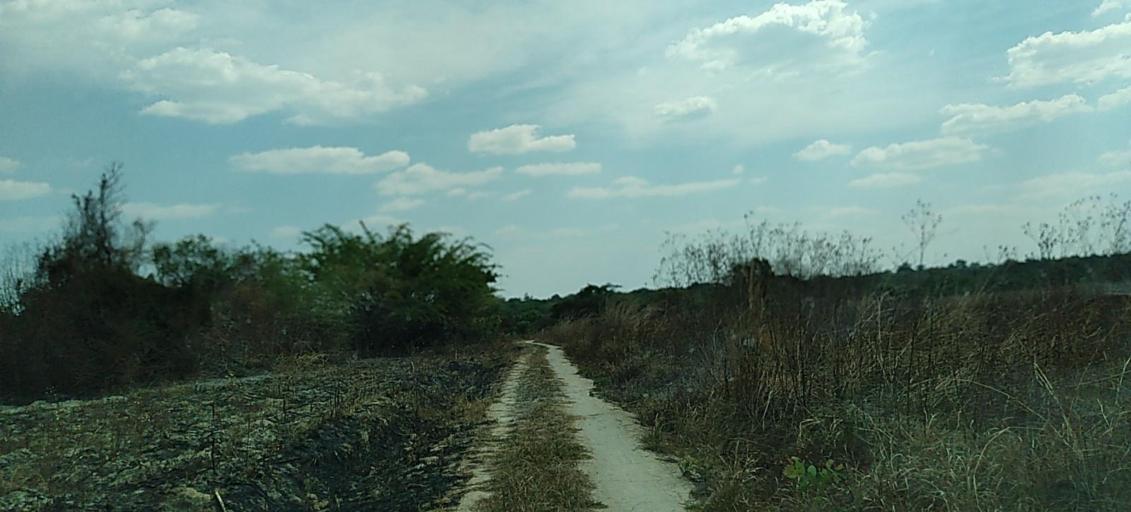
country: ZM
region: Copperbelt
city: Chililabombwe
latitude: -12.3330
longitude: 27.7857
